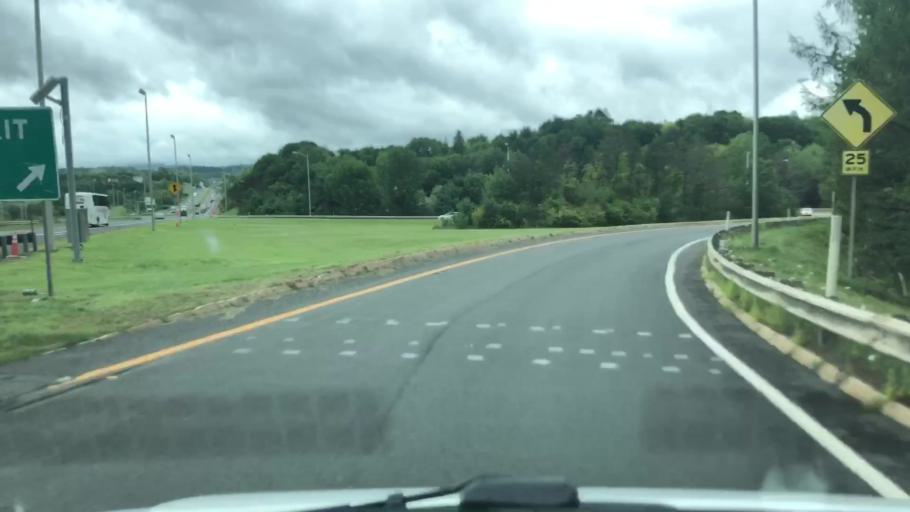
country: US
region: Massachusetts
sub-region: Berkshire County
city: Lee
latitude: 42.2991
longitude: -73.2320
